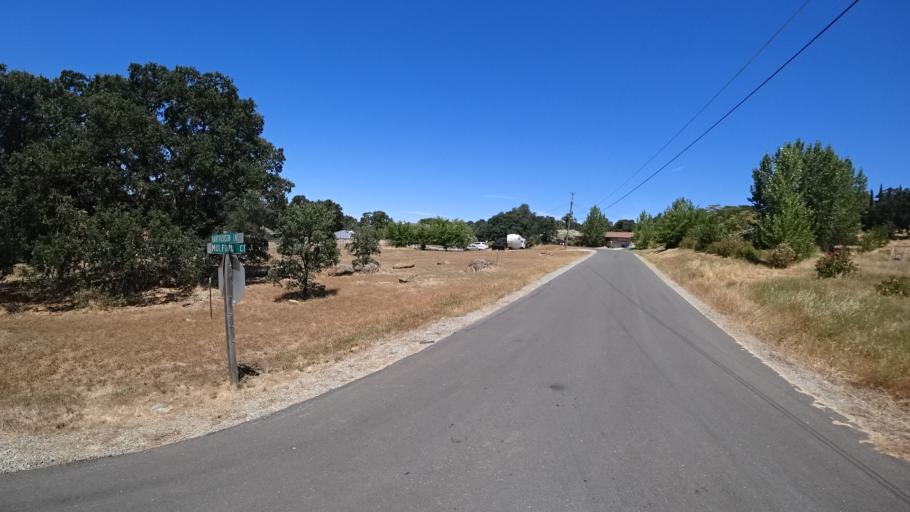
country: US
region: California
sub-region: Calaveras County
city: Rancho Calaveras
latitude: 38.1352
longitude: -120.8463
